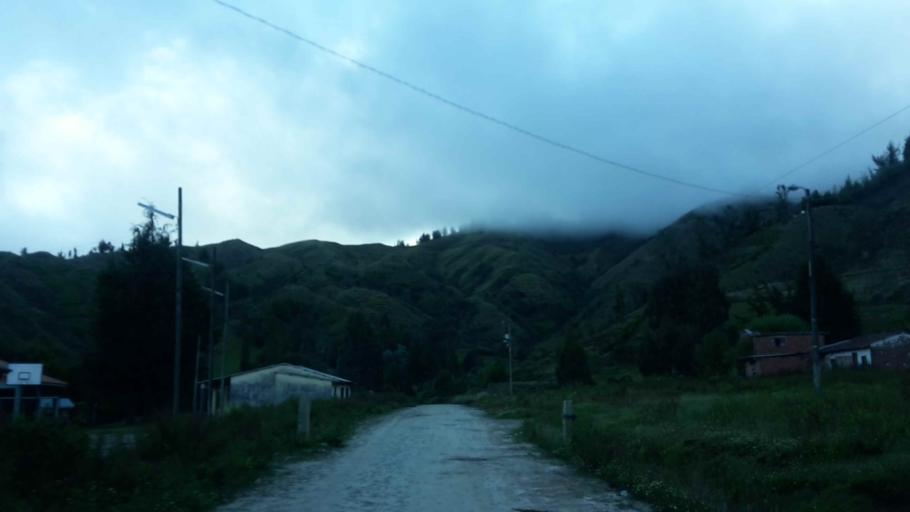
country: BO
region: Cochabamba
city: Colomi
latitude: -17.2459
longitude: -65.9058
